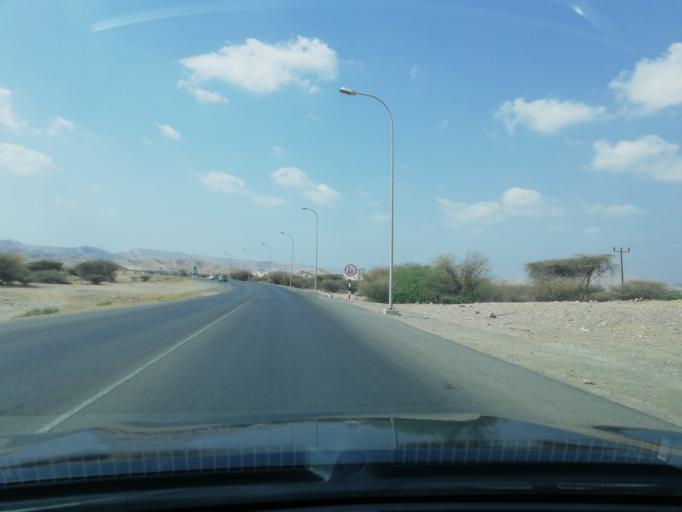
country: OM
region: Muhafazat Masqat
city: As Sib al Jadidah
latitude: 23.5870
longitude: 58.2138
